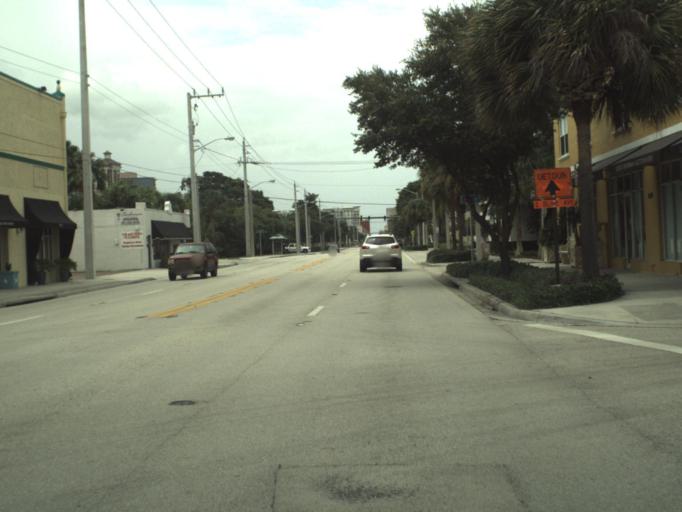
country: US
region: Florida
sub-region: Palm Beach County
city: West Palm Beach
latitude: 26.6985
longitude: -80.0540
